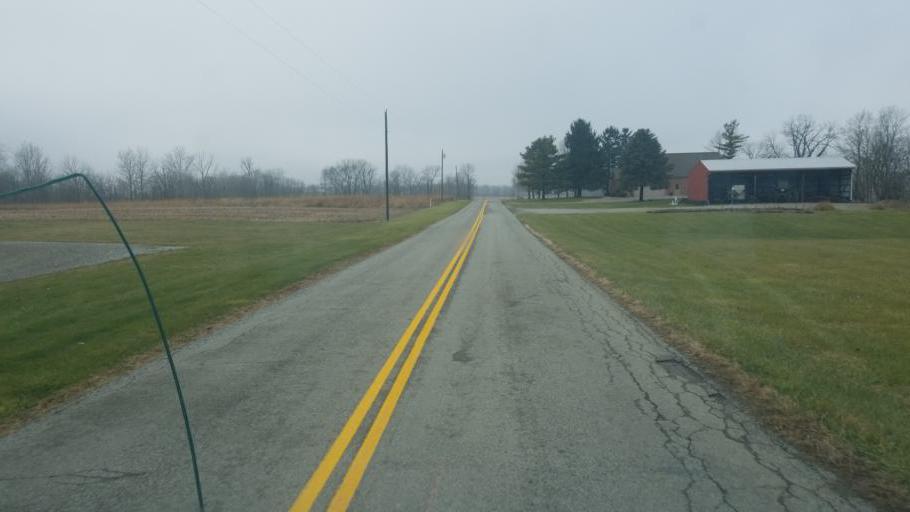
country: US
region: Ohio
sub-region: Champaign County
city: North Lewisburg
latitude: 40.2529
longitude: -83.5436
